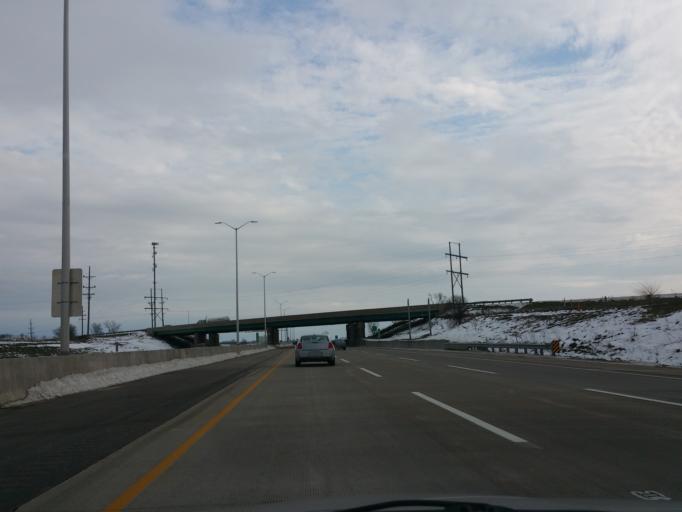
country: US
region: Illinois
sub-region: Winnebago County
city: Cherry Valley
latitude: 42.2407
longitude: -88.9193
